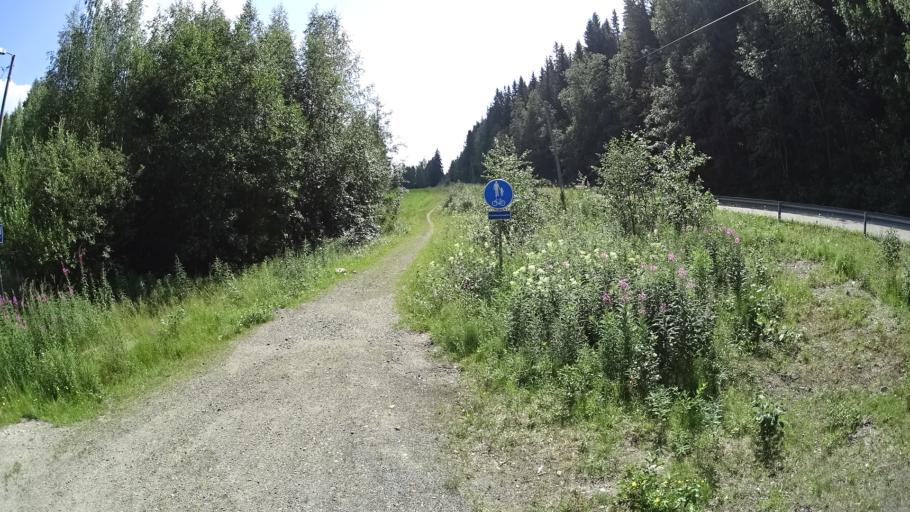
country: FI
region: North Karelia
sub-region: Pielisen Karjala
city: Lieksa
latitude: 63.1171
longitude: 29.7981
